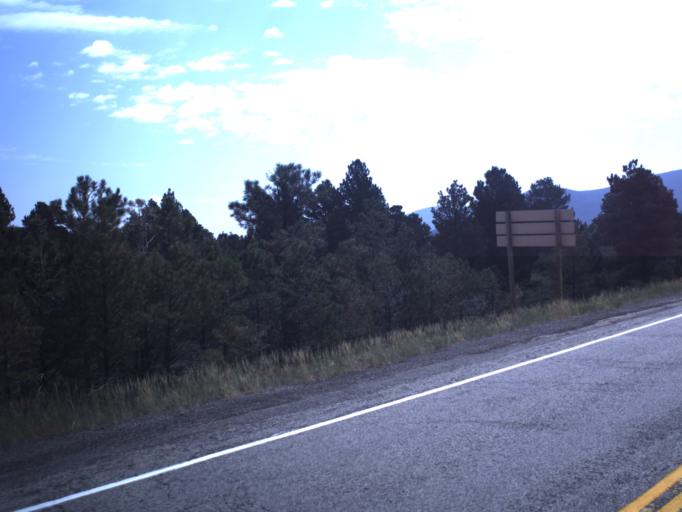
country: US
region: Utah
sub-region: Daggett County
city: Manila
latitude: 40.8654
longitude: -109.4852
